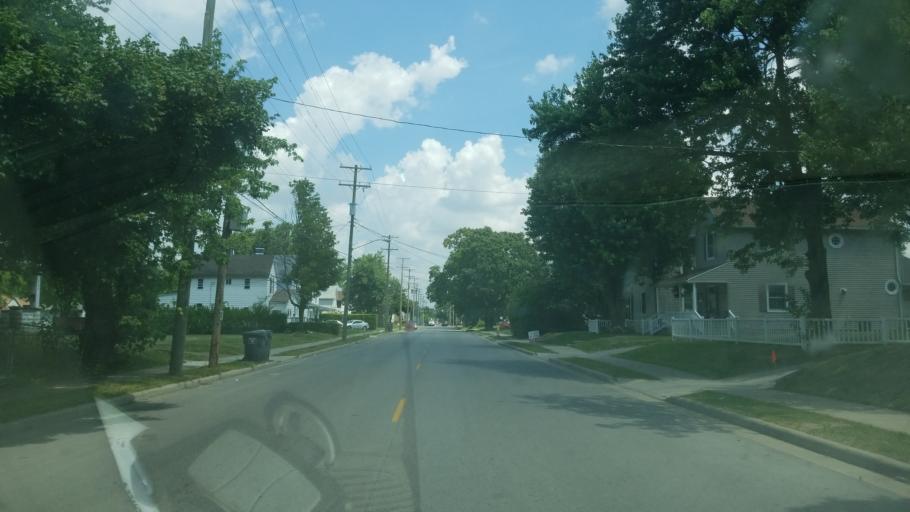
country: US
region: Ohio
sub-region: Allen County
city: Lima
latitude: 40.7277
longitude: -84.1133
